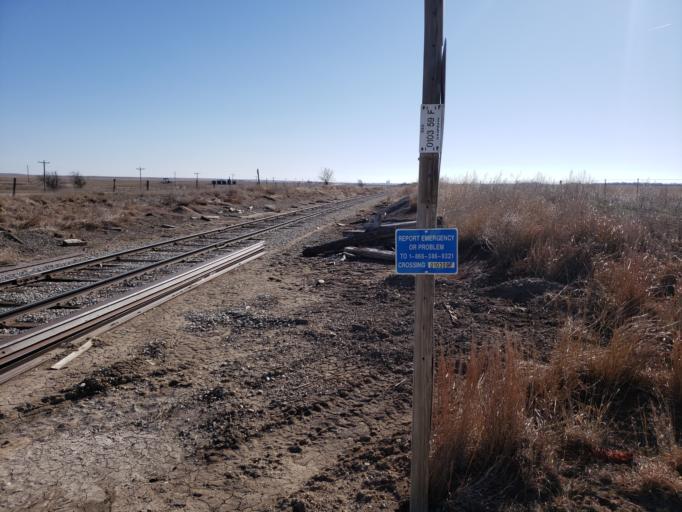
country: US
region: Kansas
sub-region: Ness County
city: Ness City
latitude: 38.4499
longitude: -100.1395
